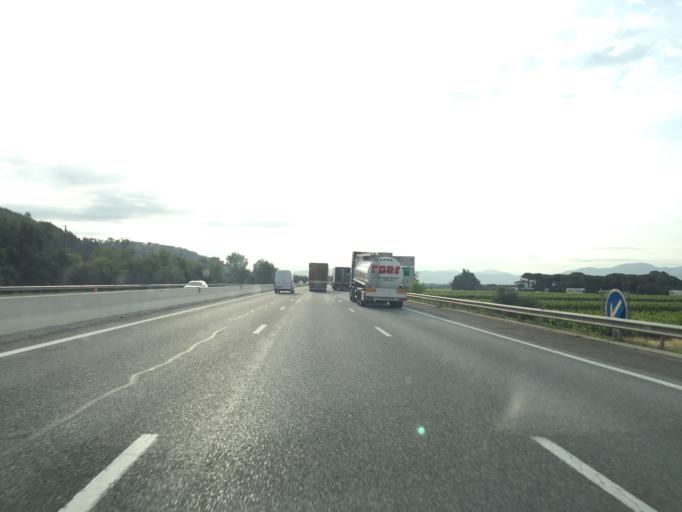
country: FR
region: Provence-Alpes-Cote d'Azur
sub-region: Departement du Var
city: Le Cannet-des-Maures
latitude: 43.4013
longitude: 6.3677
